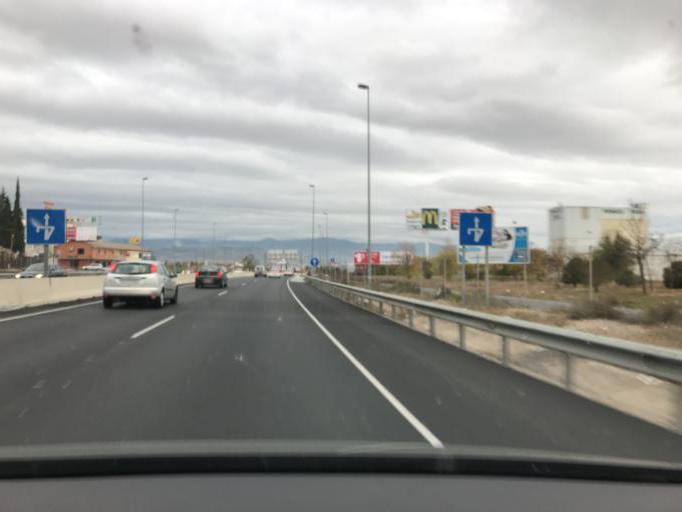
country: ES
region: Andalusia
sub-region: Provincia de Granada
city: Albolote
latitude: 37.2345
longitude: -3.6431
